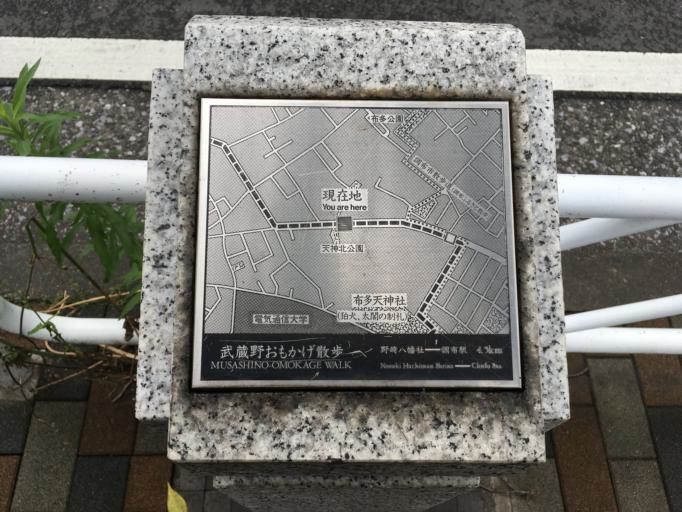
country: JP
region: Tokyo
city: Chofugaoka
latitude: 35.6582
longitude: 139.5470
